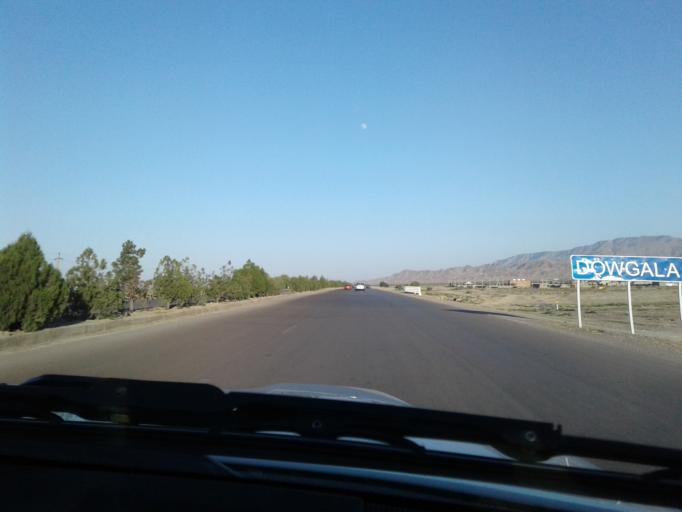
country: TM
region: Ahal
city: Baharly
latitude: 38.3085
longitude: 57.6172
